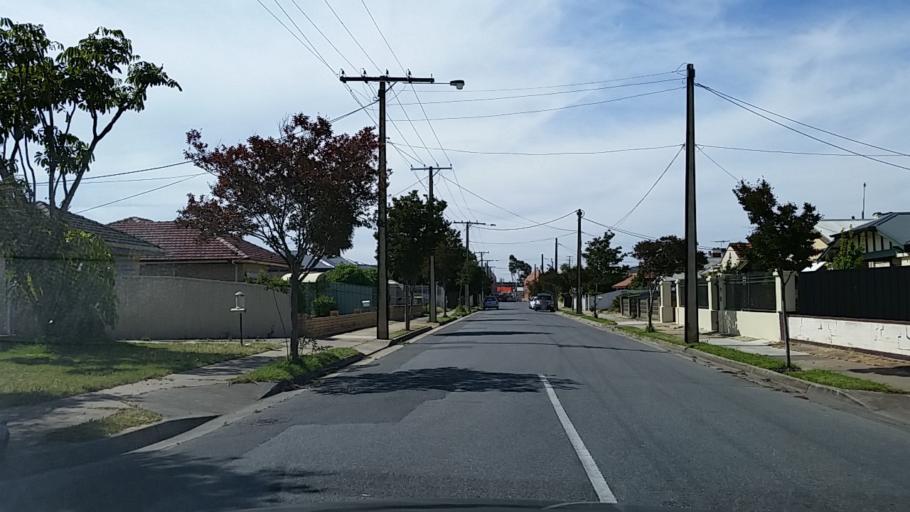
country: AU
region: South Australia
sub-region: Charles Sturt
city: Albert Park
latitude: -34.8739
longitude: 138.5199
